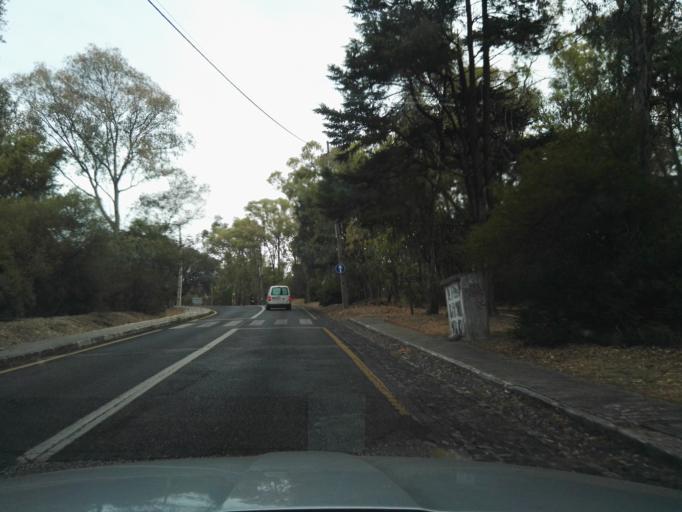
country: PT
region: Lisbon
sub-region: Odivelas
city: Pontinha
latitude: 38.7226
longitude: -9.1866
